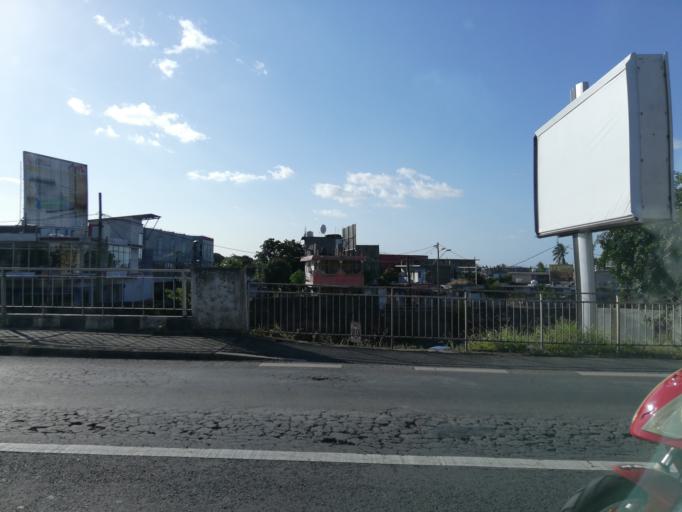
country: MU
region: Port Louis
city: Port Louis
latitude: -20.1681
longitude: 57.4852
